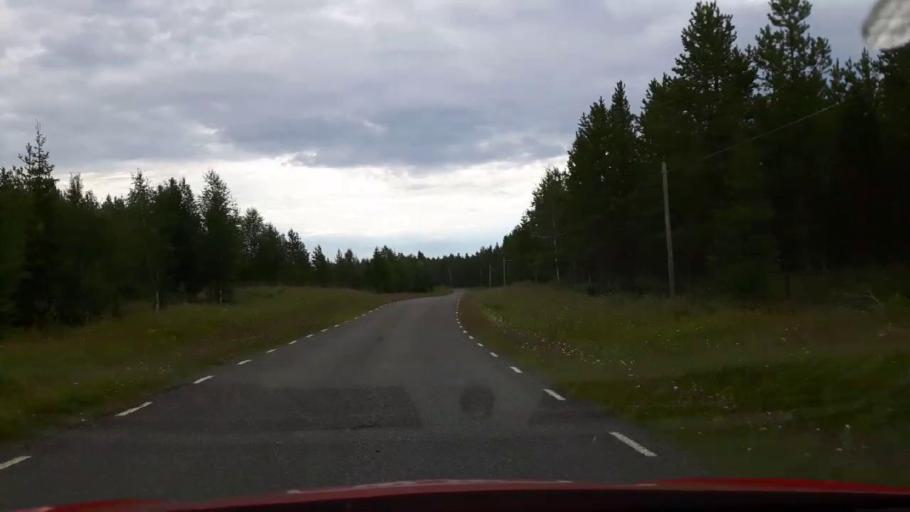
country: SE
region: Jaemtland
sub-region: OEstersunds Kommun
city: Lit
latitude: 63.3825
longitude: 15.0432
